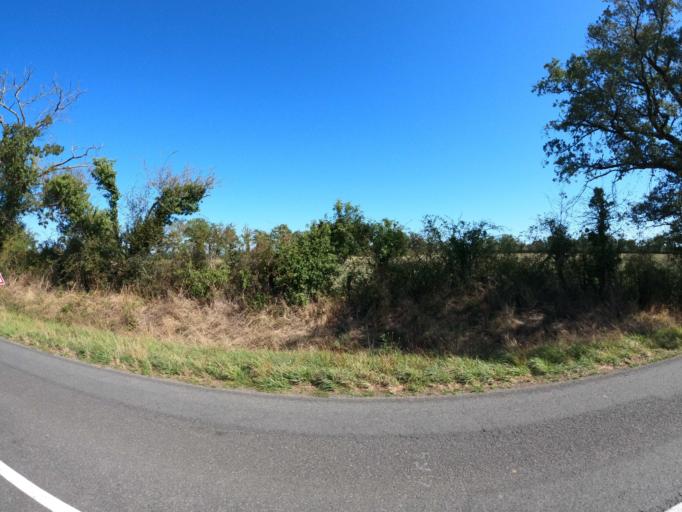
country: FR
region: Poitou-Charentes
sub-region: Departement de la Vienne
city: Lathus-Saint-Remy
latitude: 46.2988
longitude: 0.9950
